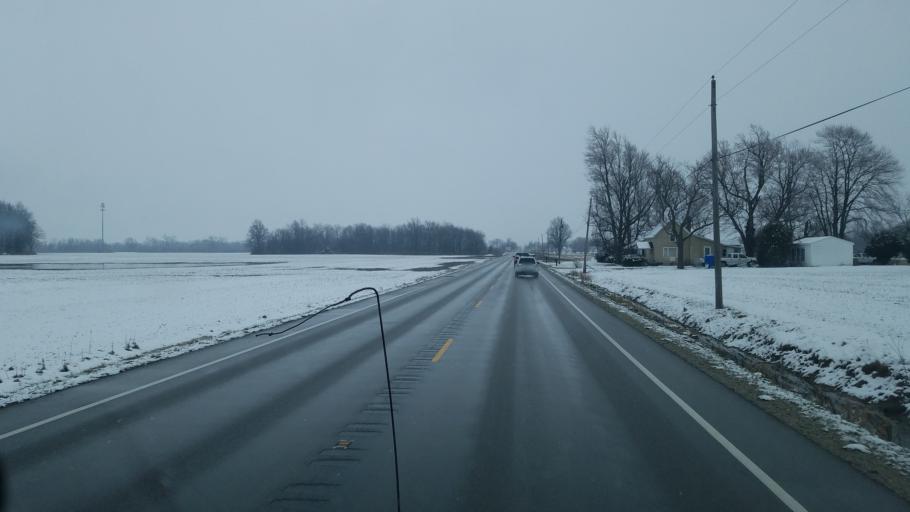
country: US
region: Indiana
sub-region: Delaware County
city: Muncie
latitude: 40.2771
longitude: -85.4491
